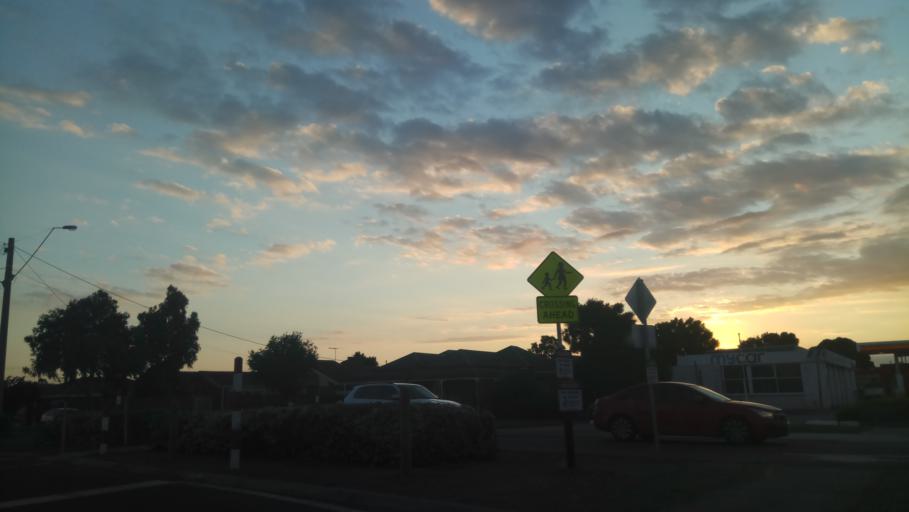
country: AU
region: Victoria
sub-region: Hobsons Bay
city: Altona Meadows
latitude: -37.8737
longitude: 144.7866
